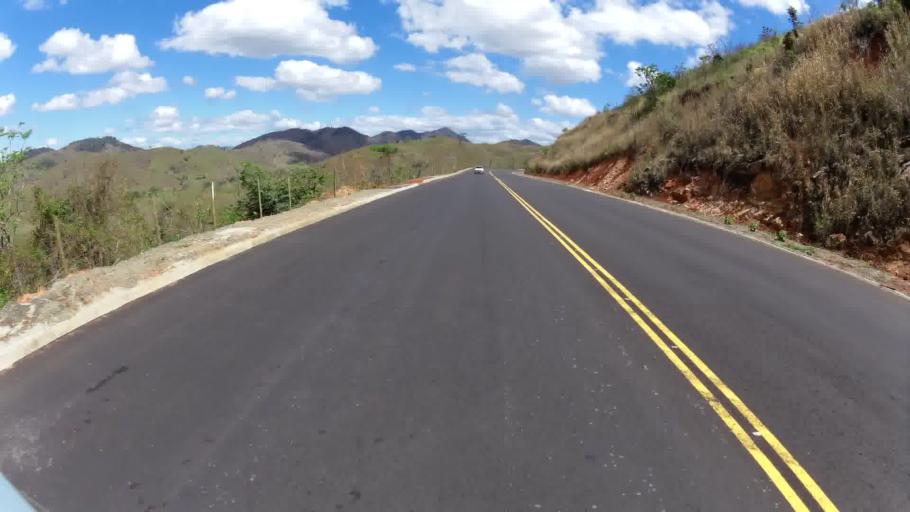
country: BR
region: Rio de Janeiro
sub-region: Itaperuna
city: Itaperuna
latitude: -21.2884
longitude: -41.8008
